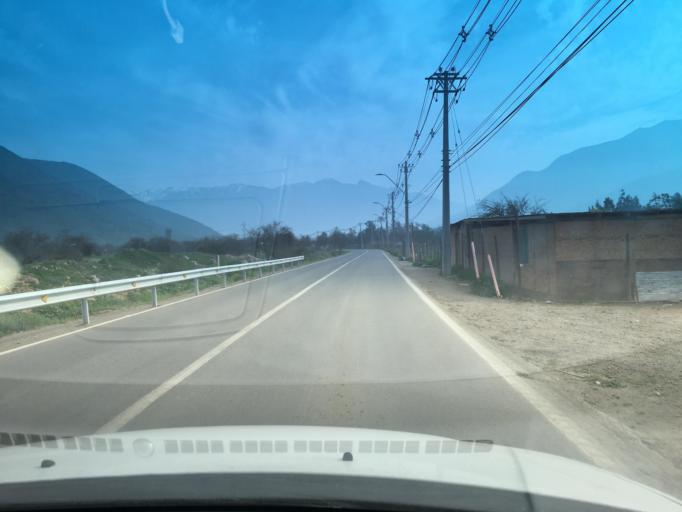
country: CL
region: Santiago Metropolitan
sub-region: Provincia de Chacabuco
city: Lampa
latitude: -33.2738
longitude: -70.8905
